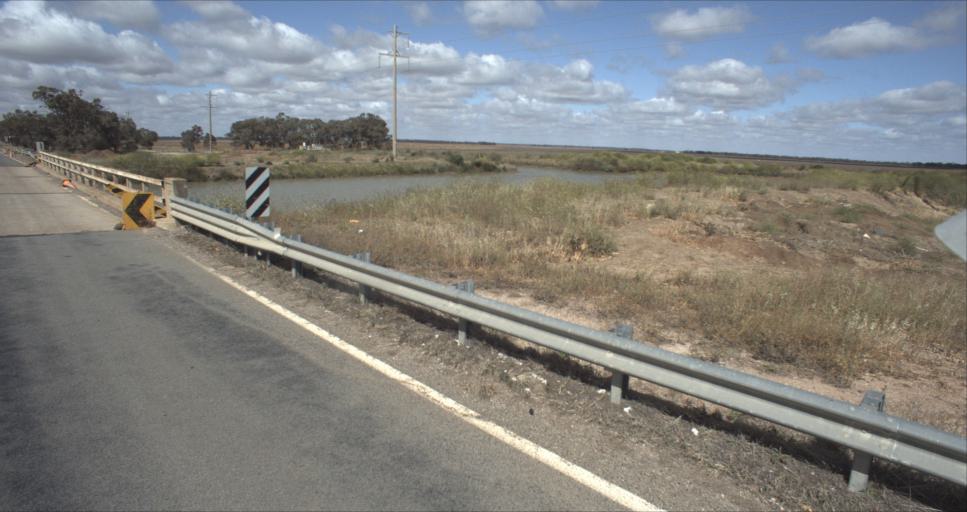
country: AU
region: New South Wales
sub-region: Murrumbidgee Shire
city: Darlington Point
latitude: -34.5526
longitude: 146.1704
